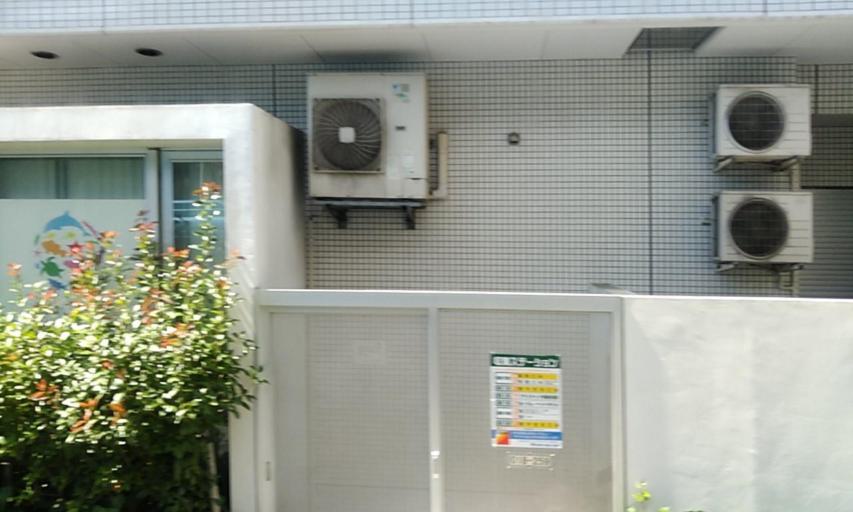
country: JP
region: Kagawa
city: Takamatsu-shi
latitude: 34.3367
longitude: 134.0519
